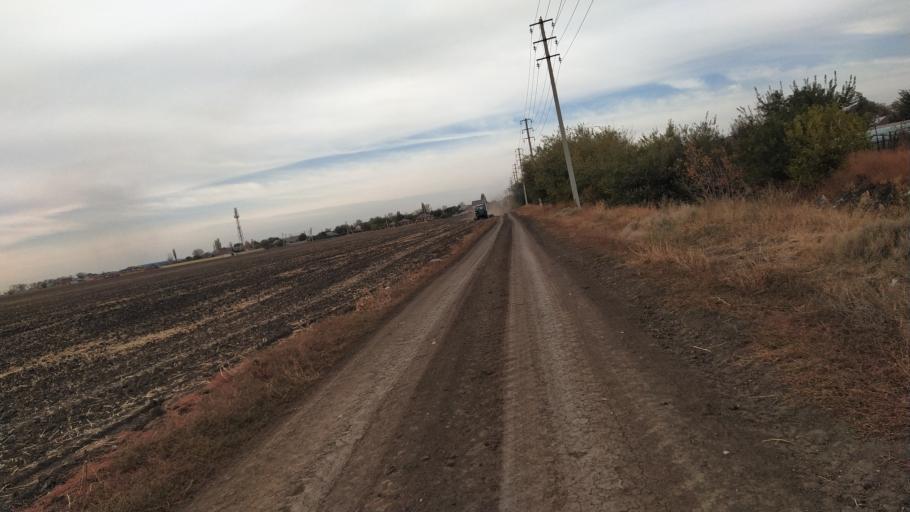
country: RU
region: Rostov
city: Bataysk
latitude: 47.1095
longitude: 39.6836
